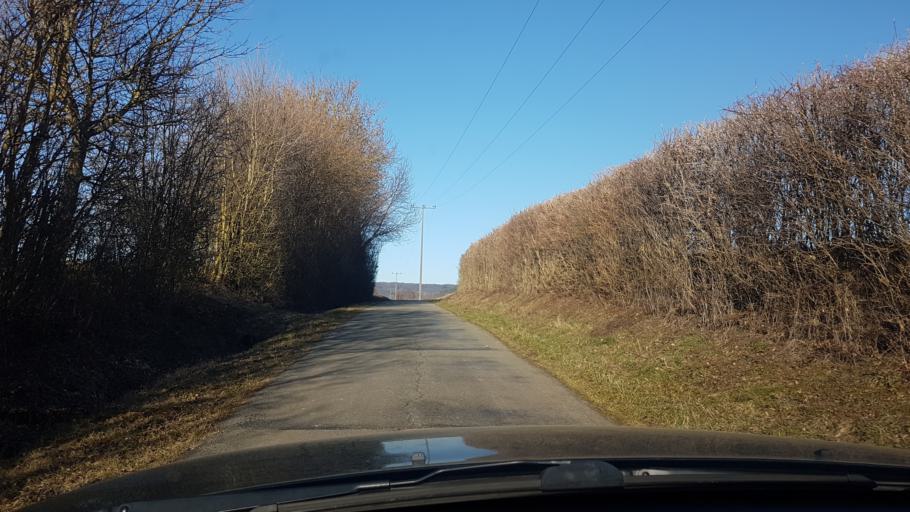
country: DE
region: Bavaria
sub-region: Upper Franconia
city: Ebensfeld
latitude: 50.0231
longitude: 10.9971
